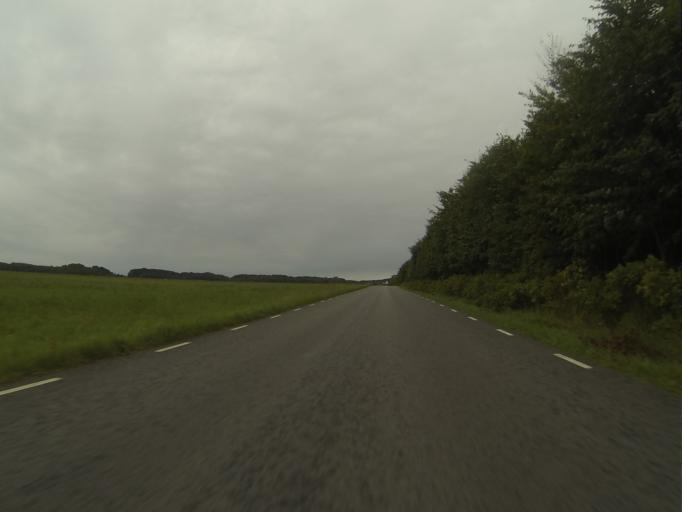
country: SE
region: Skane
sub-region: Lunds Kommun
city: Veberod
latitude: 55.6734
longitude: 13.4331
